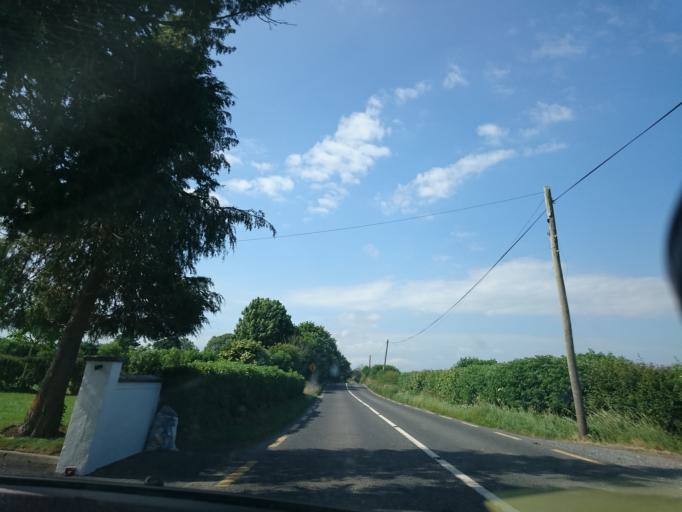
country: IE
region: Leinster
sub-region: Kilkenny
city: Kilkenny
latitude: 52.5616
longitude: -7.2275
